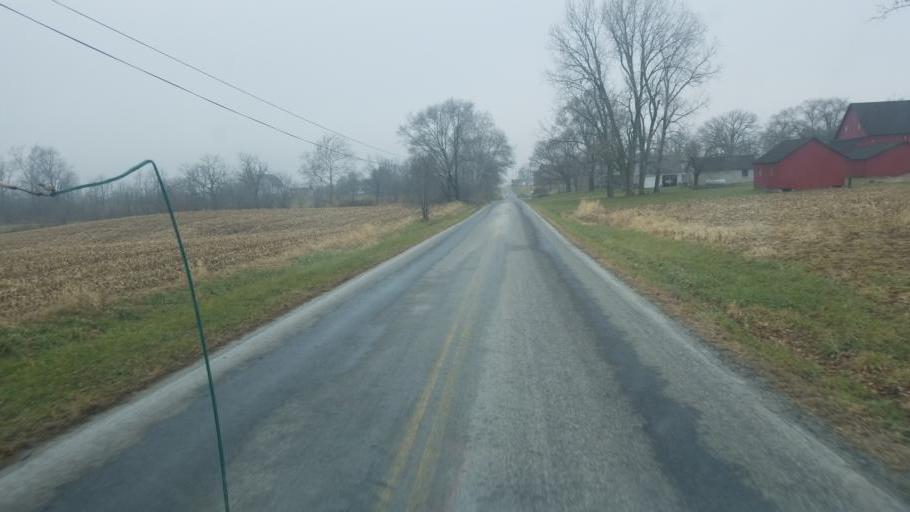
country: US
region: Ohio
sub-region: Hardin County
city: Kenton
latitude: 40.5674
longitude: -83.4679
